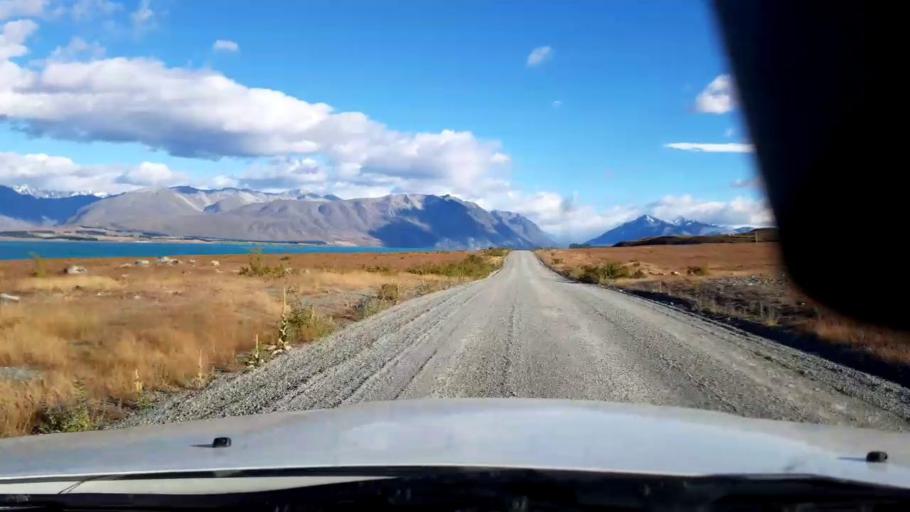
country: NZ
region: Canterbury
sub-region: Timaru District
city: Pleasant Point
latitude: -43.9179
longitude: 170.5585
